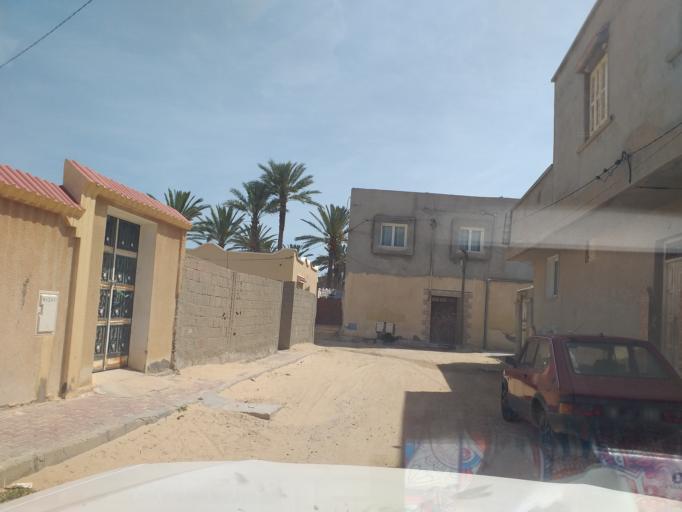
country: TN
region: Qabis
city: Gabes
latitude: 33.9419
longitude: 10.0703
